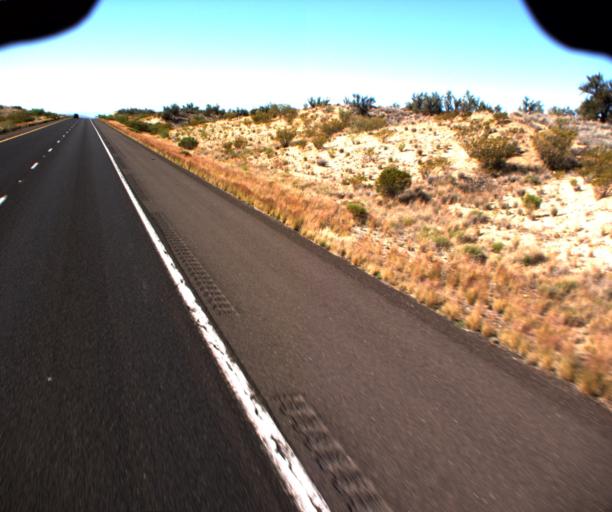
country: US
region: Arizona
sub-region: Mohave County
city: Kingman
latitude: 35.0935
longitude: -113.6663
